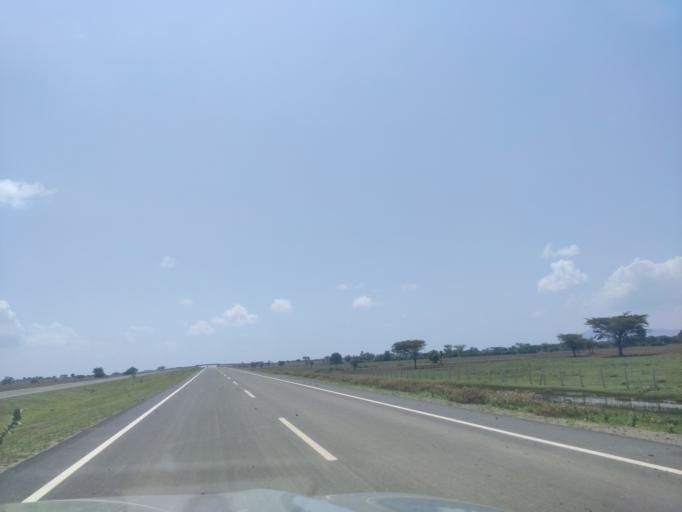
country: ET
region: Oromiya
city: Ziway
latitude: 8.2356
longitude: 38.8772
